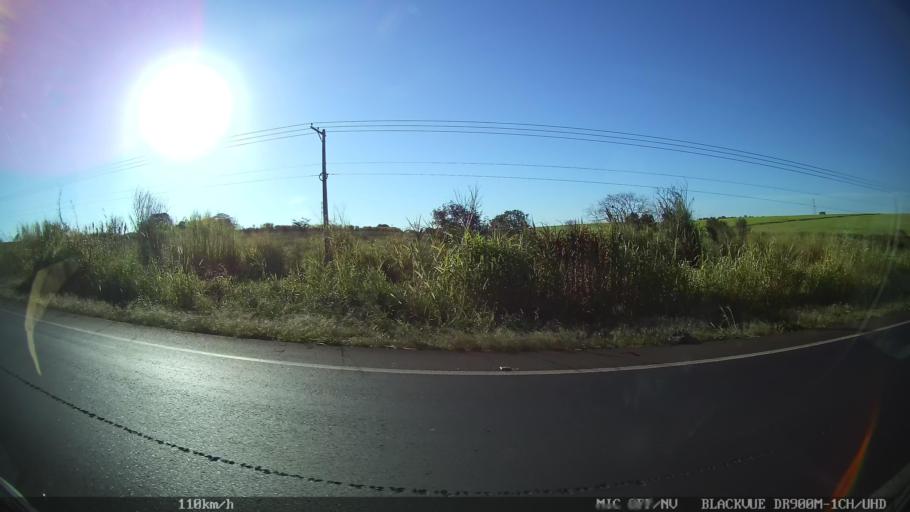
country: BR
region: Sao Paulo
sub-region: Olimpia
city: Olimpia
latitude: -20.7307
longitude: -49.0561
